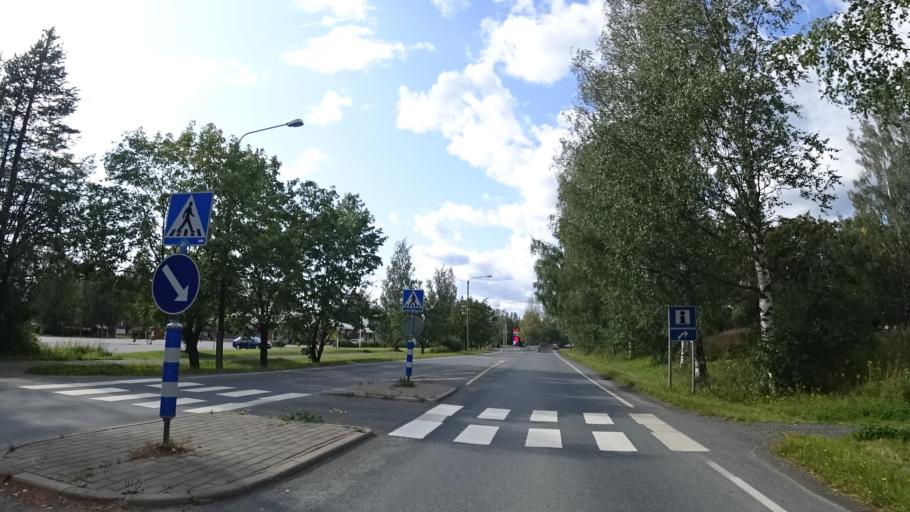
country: FI
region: North Karelia
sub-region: Keski-Karjala
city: Tohmajaervi
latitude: 62.2244
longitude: 30.3380
